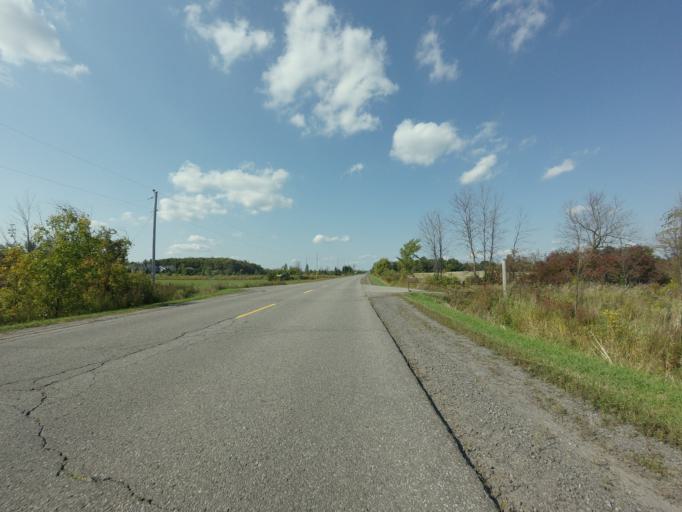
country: CA
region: Ontario
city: Ottawa
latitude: 45.2433
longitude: -75.6747
